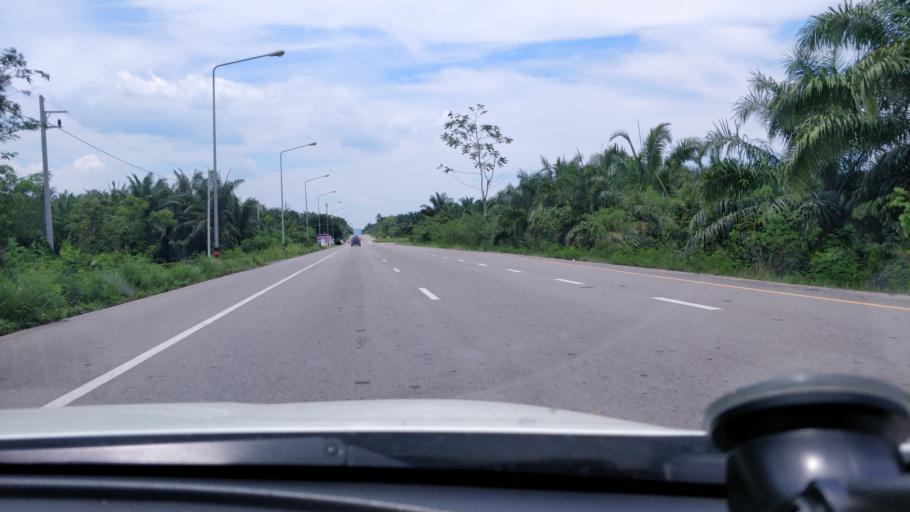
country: TH
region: Krabi
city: Plai Phraya
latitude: 8.5047
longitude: 98.8857
